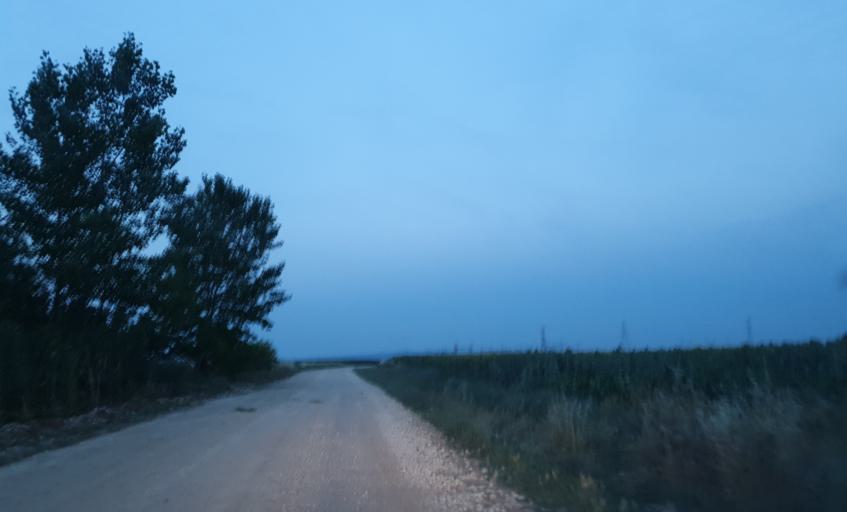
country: TR
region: Kirklareli
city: Vize
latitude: 41.5182
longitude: 27.7492
